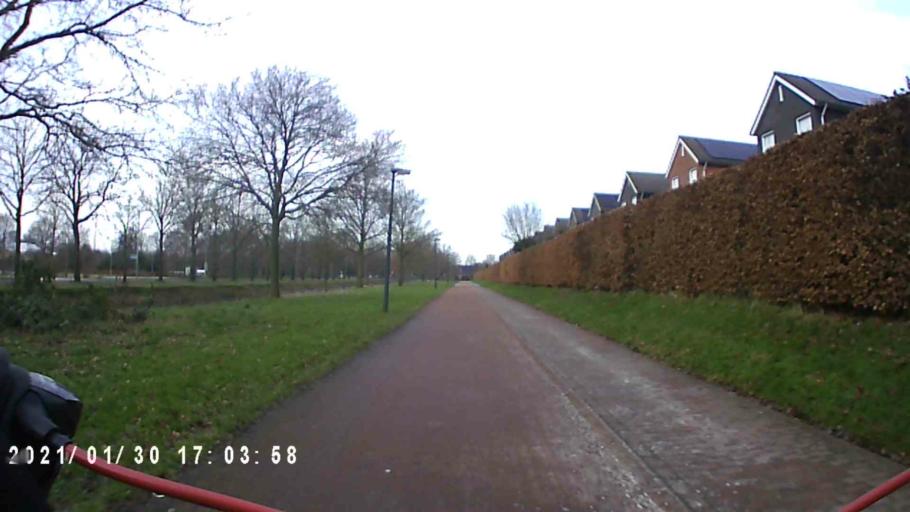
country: NL
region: Groningen
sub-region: Gemeente Leek
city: Leek
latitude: 53.1556
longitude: 6.3702
